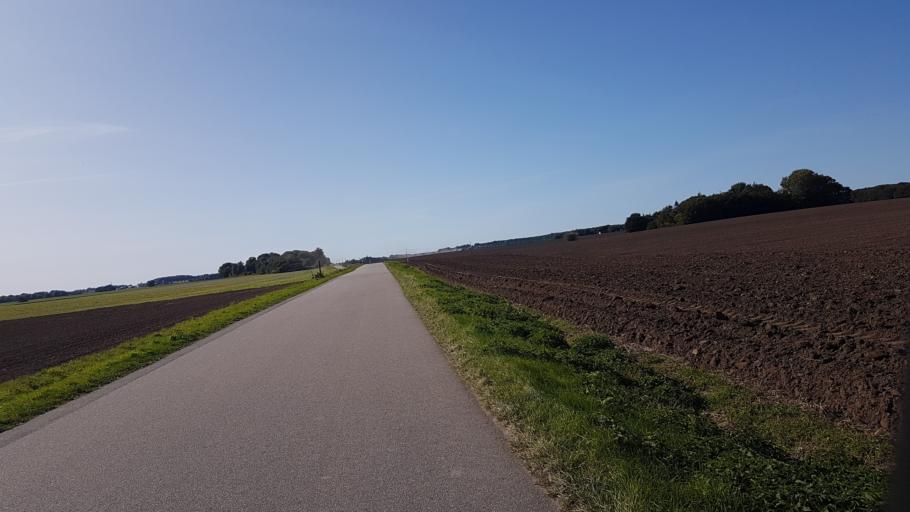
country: DE
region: Mecklenburg-Vorpommern
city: Altenkirchen
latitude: 54.6595
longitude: 13.3253
